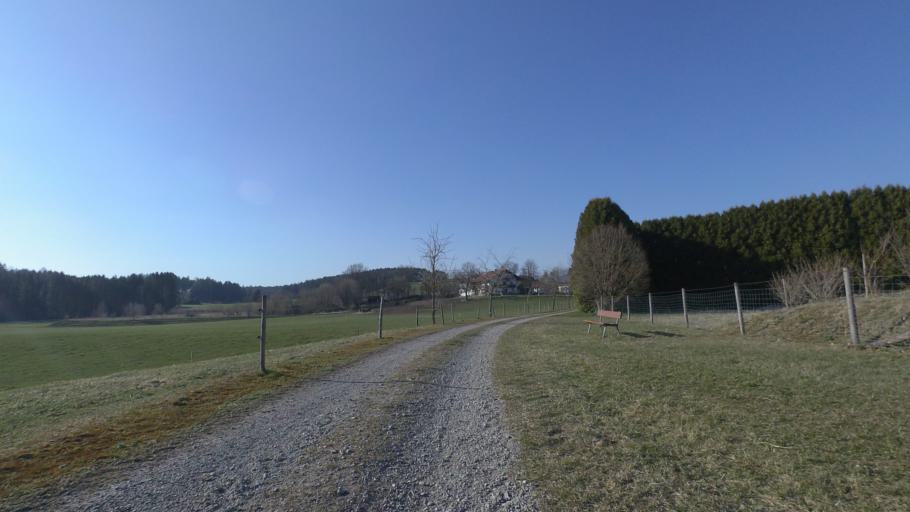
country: DE
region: Bavaria
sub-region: Upper Bavaria
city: Chieming
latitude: 47.9411
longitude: 12.5464
